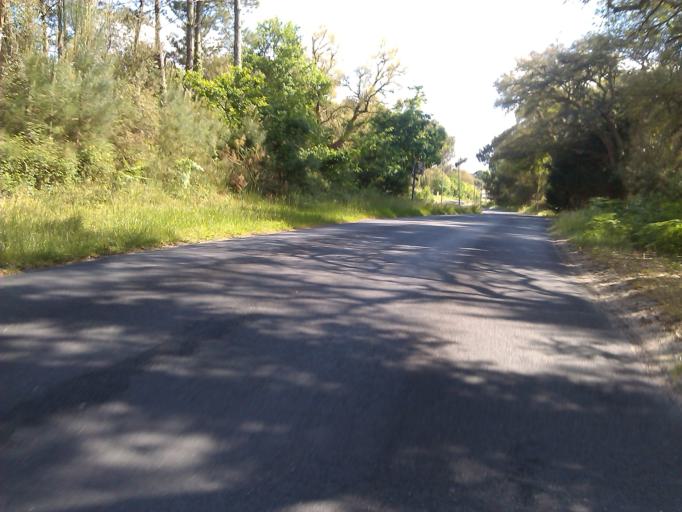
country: FR
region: Aquitaine
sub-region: Departement des Landes
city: Leon
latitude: 43.8566
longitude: -1.3582
